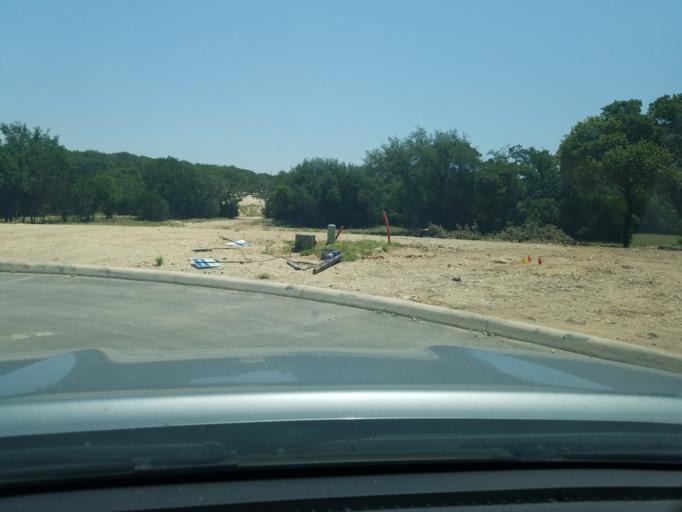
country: US
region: Texas
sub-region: Bexar County
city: Timberwood Park
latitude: 29.7139
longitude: -98.5060
